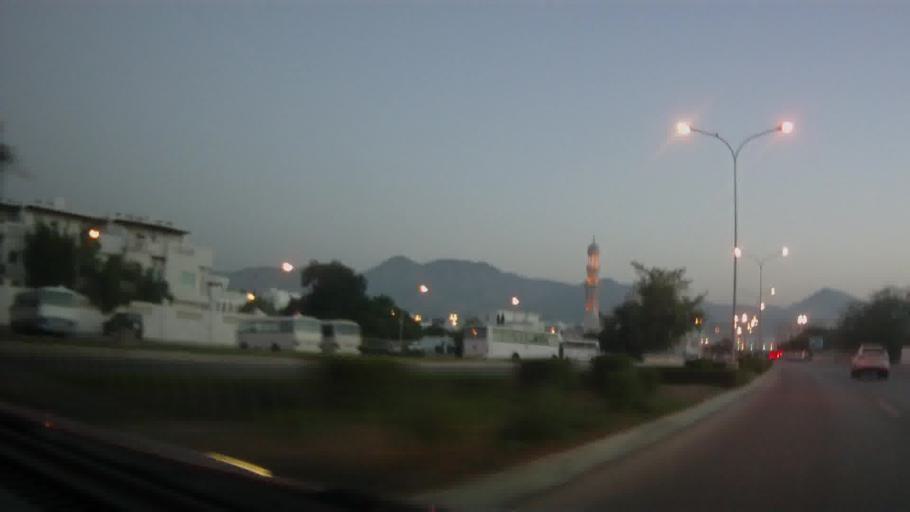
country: OM
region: Muhafazat Masqat
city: Bawshar
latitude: 23.6035
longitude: 58.4419
